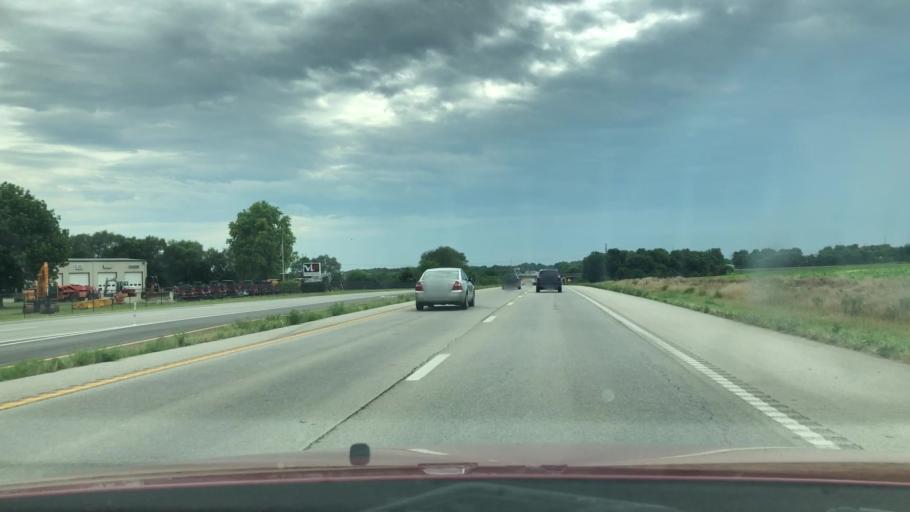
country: US
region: Missouri
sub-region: Greene County
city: Battlefield
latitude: 37.1527
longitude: -93.4161
